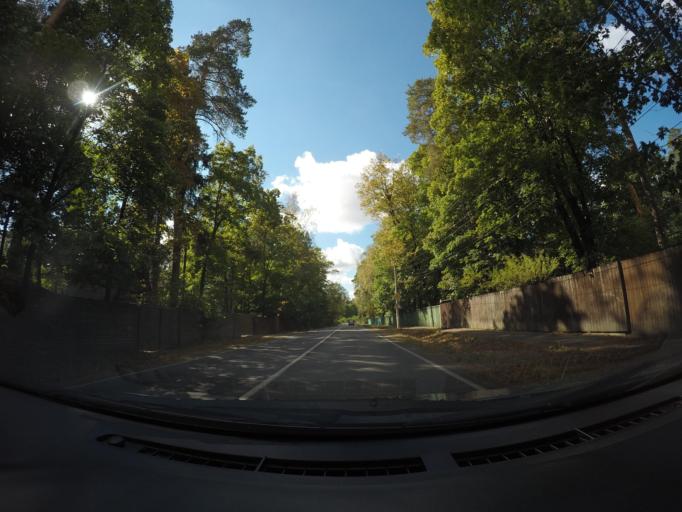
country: RU
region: Moskovskaya
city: Il'inskiy
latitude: 55.6104
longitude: 38.1368
